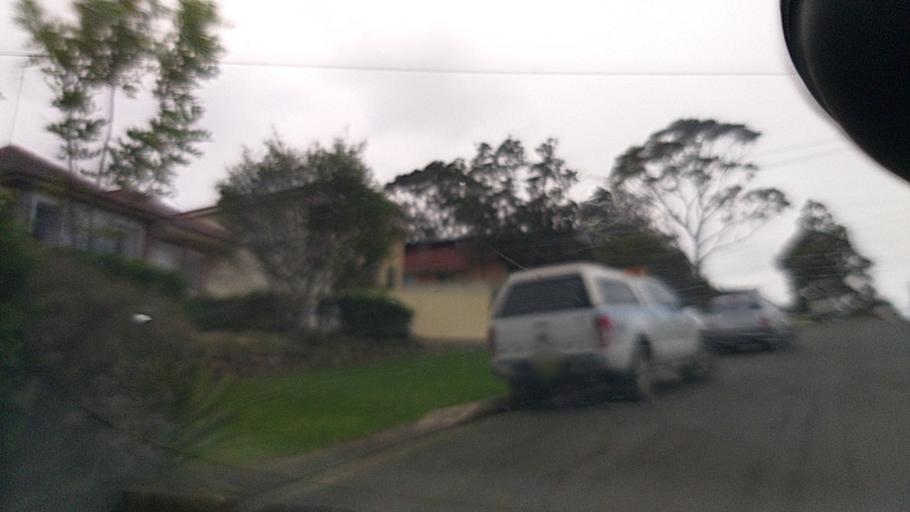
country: AU
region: New South Wales
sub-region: Wollongong
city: Mount Saint Thomas
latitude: -34.4406
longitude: 150.8711
